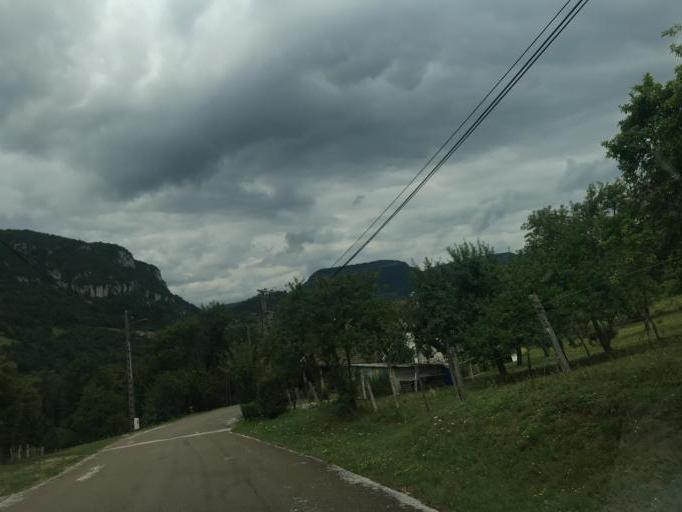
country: FR
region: Franche-Comte
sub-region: Departement du Jura
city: Saint-Claude
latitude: 46.3589
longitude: 5.8601
